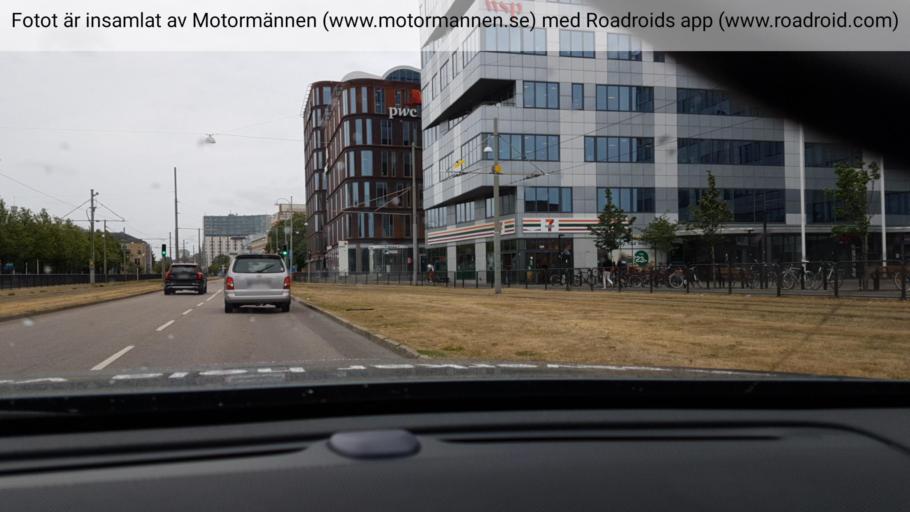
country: SE
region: Vaestra Goetaland
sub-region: Goteborg
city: Goeteborg
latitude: 57.7071
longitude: 11.9846
